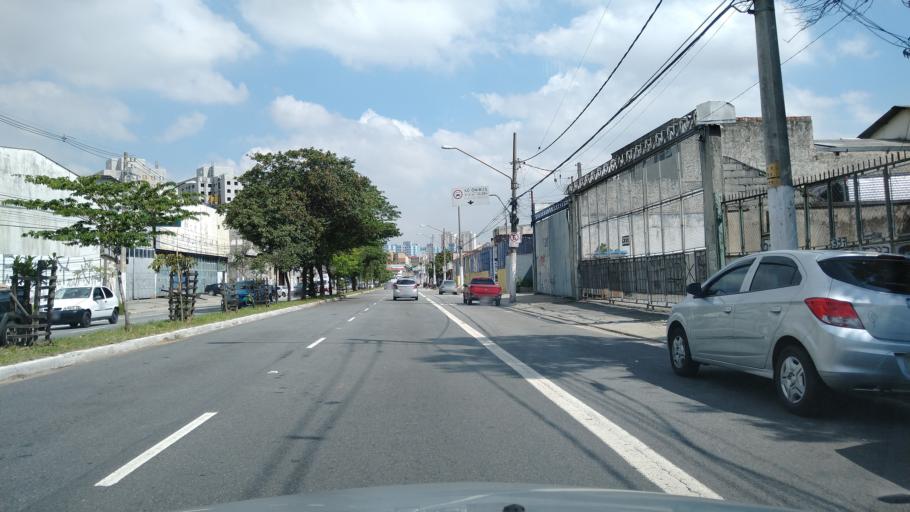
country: BR
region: Sao Paulo
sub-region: Guarulhos
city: Guarulhos
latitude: -23.4902
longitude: -46.5053
